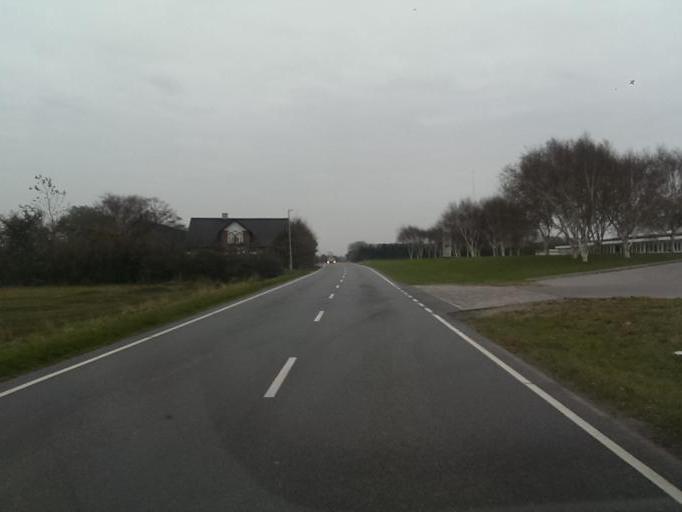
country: DK
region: South Denmark
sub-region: Esbjerg Kommune
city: Tjaereborg
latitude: 55.4599
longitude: 8.5685
